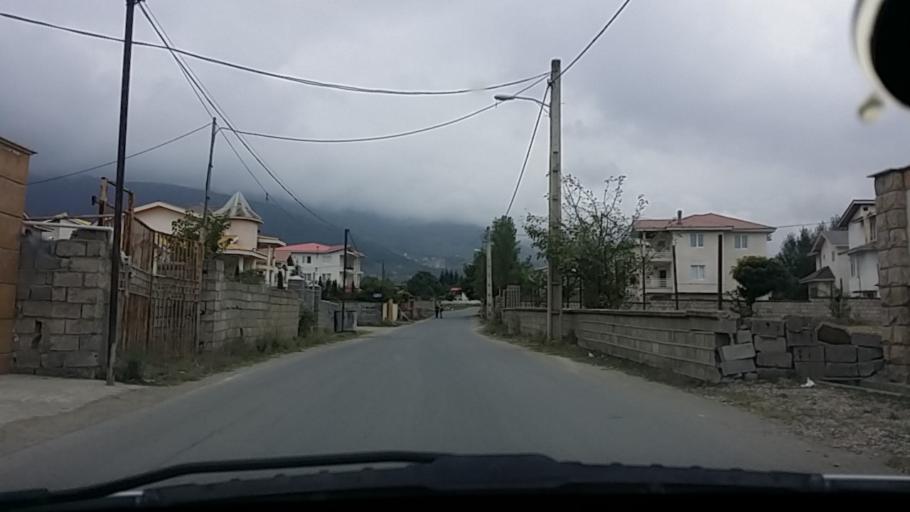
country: IR
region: Mazandaran
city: `Abbasabad
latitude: 36.5115
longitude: 51.1700
